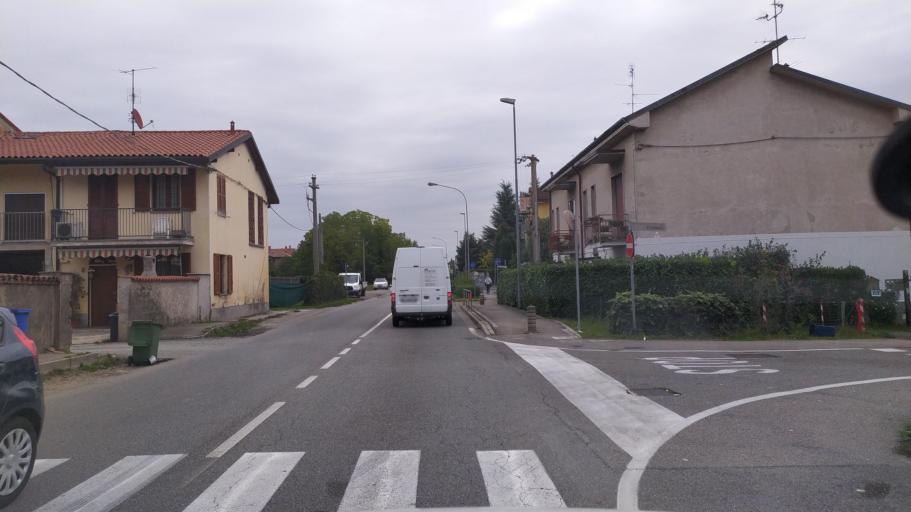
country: IT
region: Lombardy
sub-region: Provincia di Monza e Brianza
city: Desio
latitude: 45.6230
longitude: 9.1811
